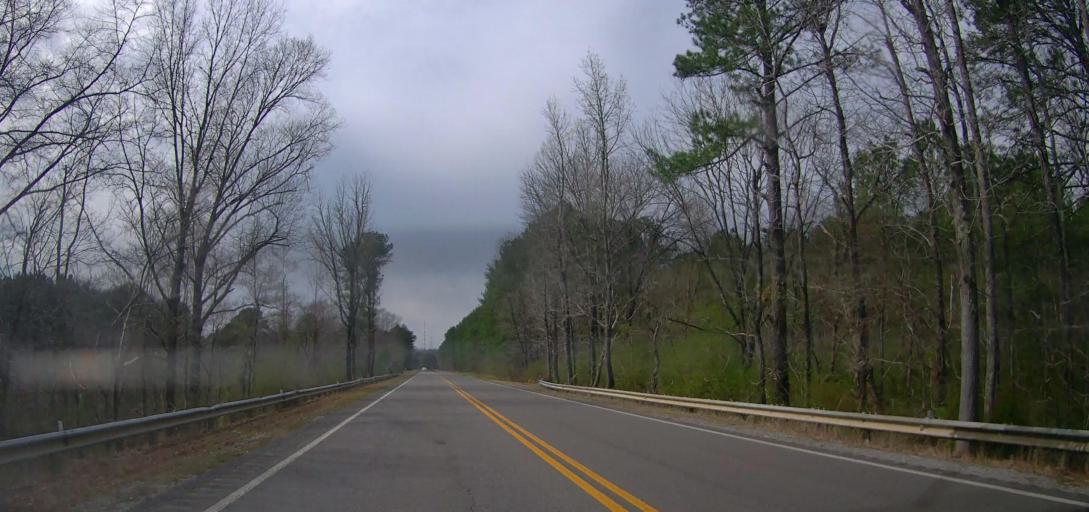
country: US
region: Alabama
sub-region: Walker County
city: Carbon Hill
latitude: 33.8985
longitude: -87.5402
